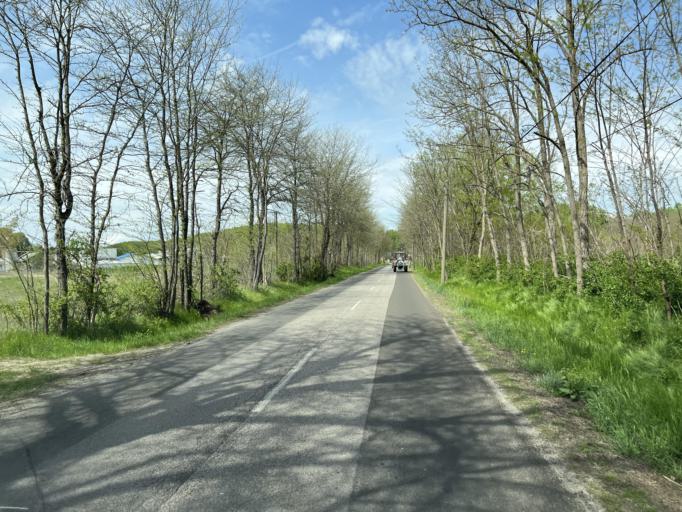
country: HU
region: Pest
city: Albertirsa
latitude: 47.2179
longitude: 19.6094
